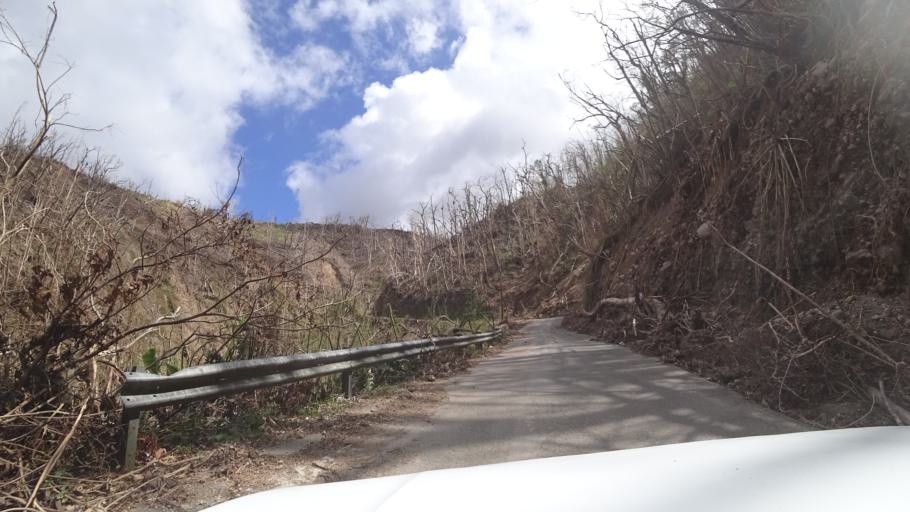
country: DM
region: Saint Luke
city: Pointe Michel
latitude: 15.2668
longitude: -61.3504
